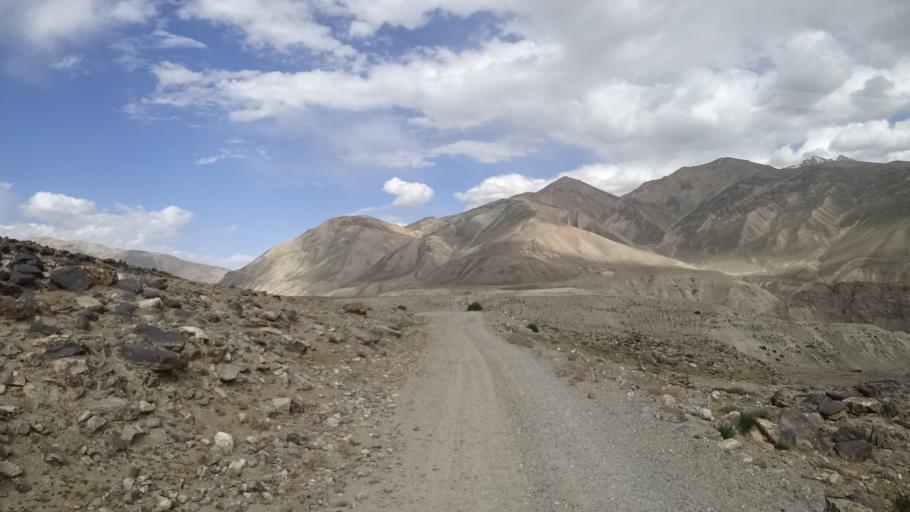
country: AF
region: Badakhshan
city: Khandud
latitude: 37.1886
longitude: 72.7595
